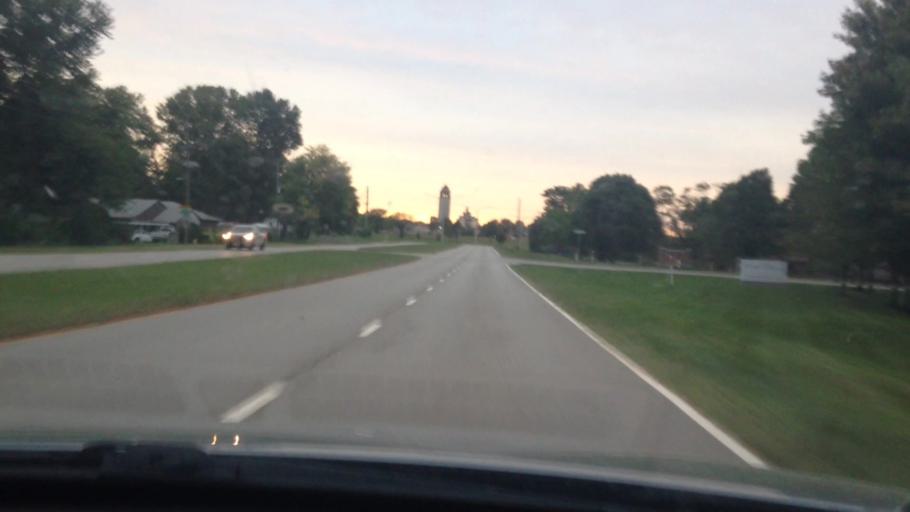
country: US
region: Missouri
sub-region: Jackson County
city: Lees Summit
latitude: 38.9384
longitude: -94.4042
